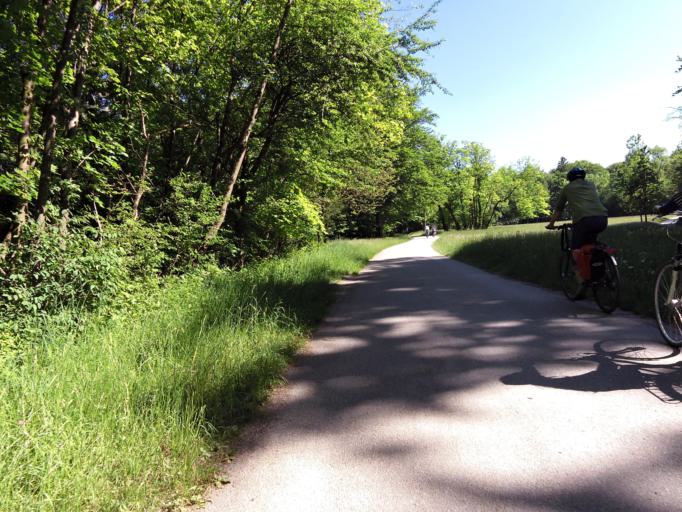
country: DE
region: Bavaria
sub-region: Upper Bavaria
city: Unterfoehring
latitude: 48.1836
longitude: 11.6199
